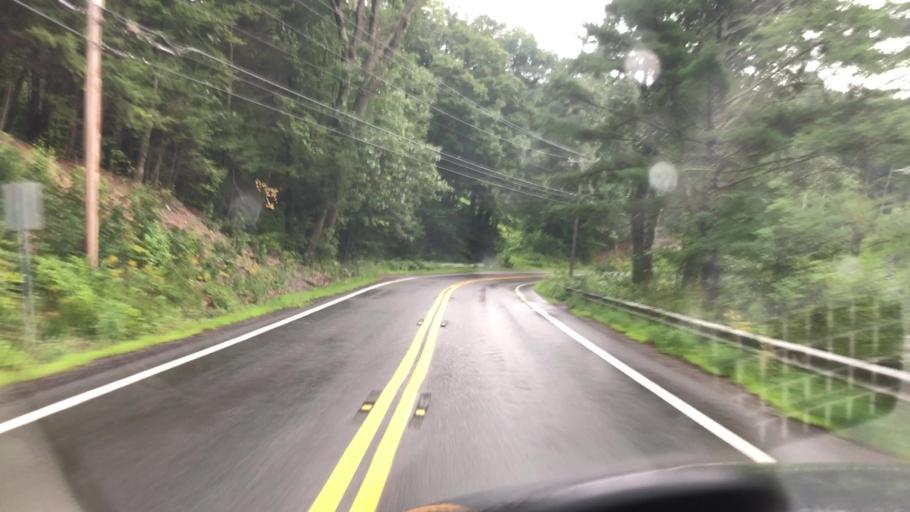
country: US
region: Massachusetts
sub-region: Hampshire County
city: Westhampton
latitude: 42.2749
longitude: -72.8619
